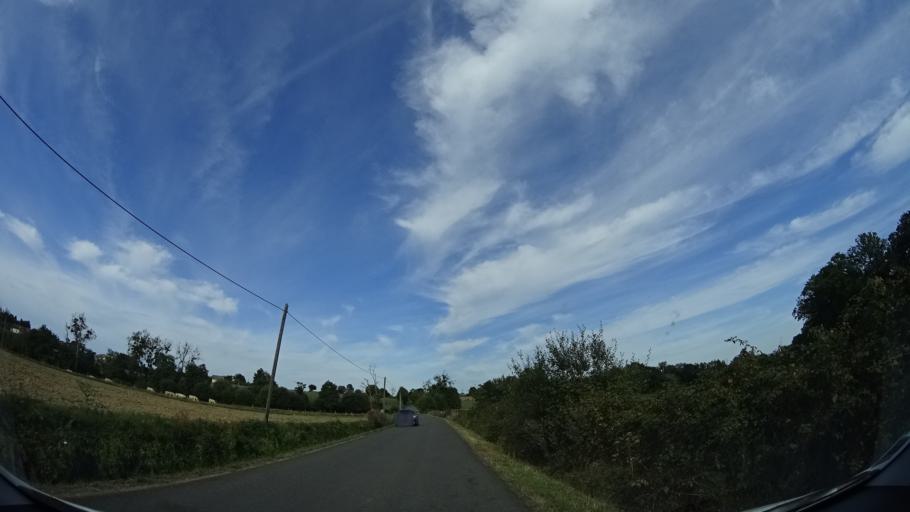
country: FR
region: Brittany
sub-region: Departement d'Ille-et-Vilaine
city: Javene
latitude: 48.3370
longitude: -1.2343
